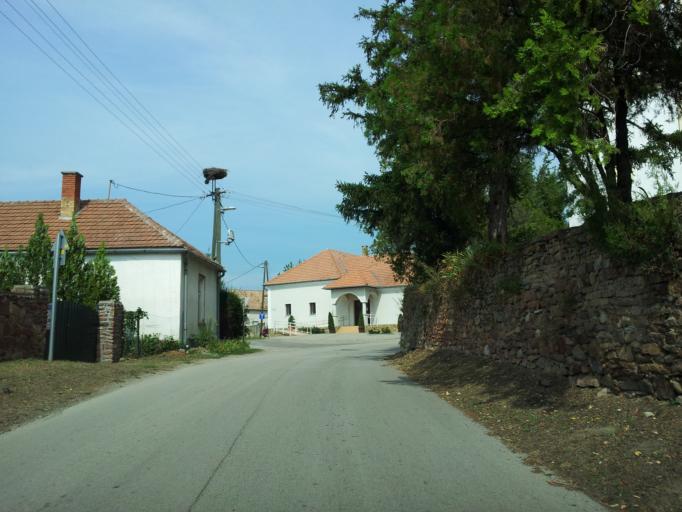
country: HU
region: Veszprem
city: Badacsonytomaj
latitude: 46.8506
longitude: 17.5137
